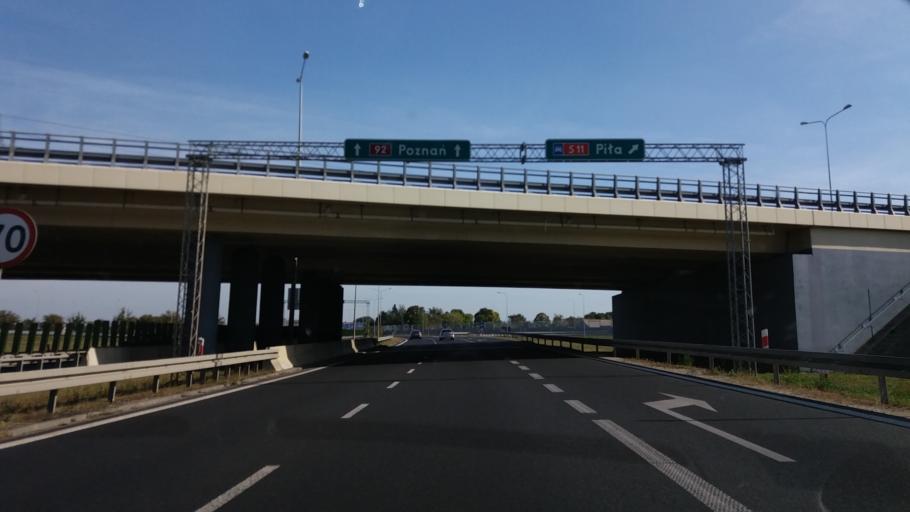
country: PL
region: Greater Poland Voivodeship
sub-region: Powiat poznanski
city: Baranowo
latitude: 52.4428
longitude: 16.7397
